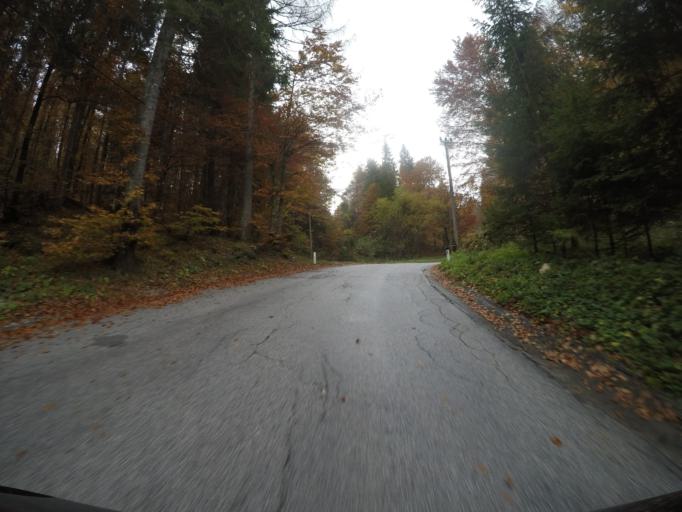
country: SI
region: Kranjska Gora
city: Mojstrana
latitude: 46.4398
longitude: 13.9317
